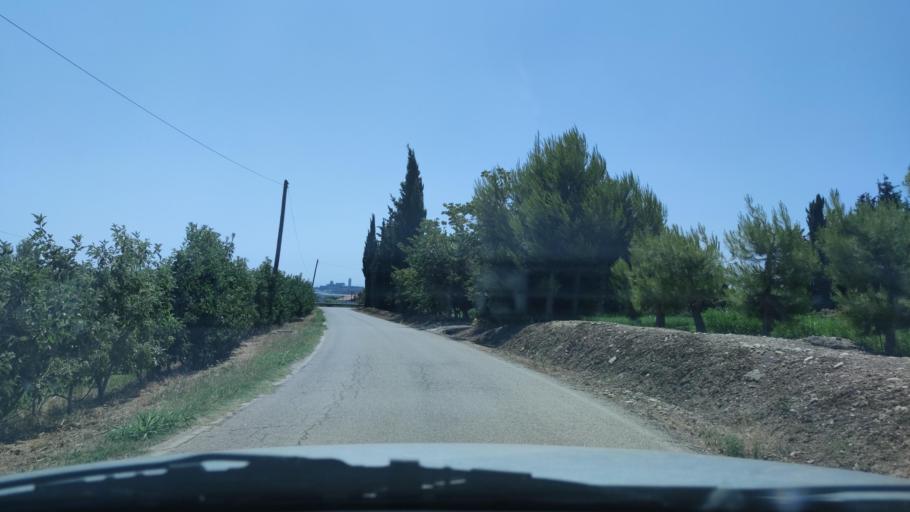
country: ES
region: Catalonia
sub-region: Provincia de Lleida
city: Lleida
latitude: 41.6380
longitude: 0.5969
